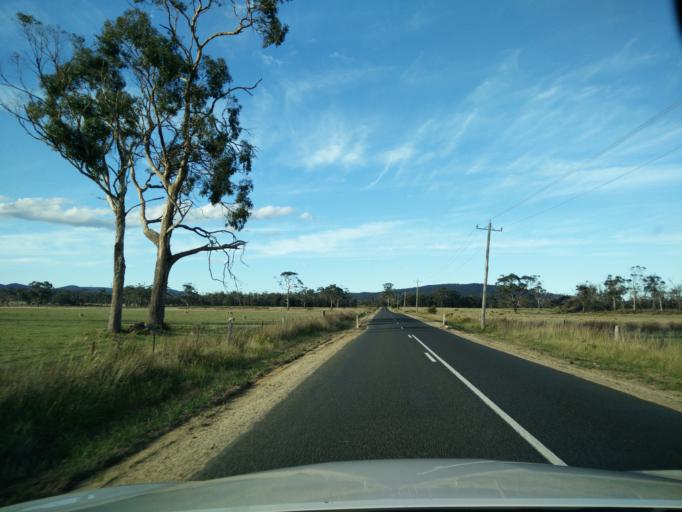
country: AU
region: Tasmania
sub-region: Break O'Day
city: St Helens
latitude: -41.9054
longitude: 148.2535
